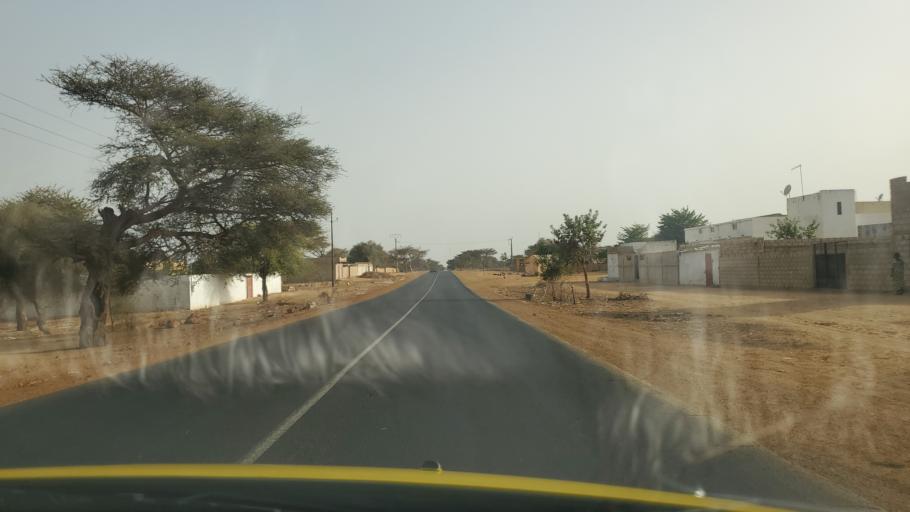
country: SN
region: Thies
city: Mekhe
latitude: 15.2144
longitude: -16.5694
